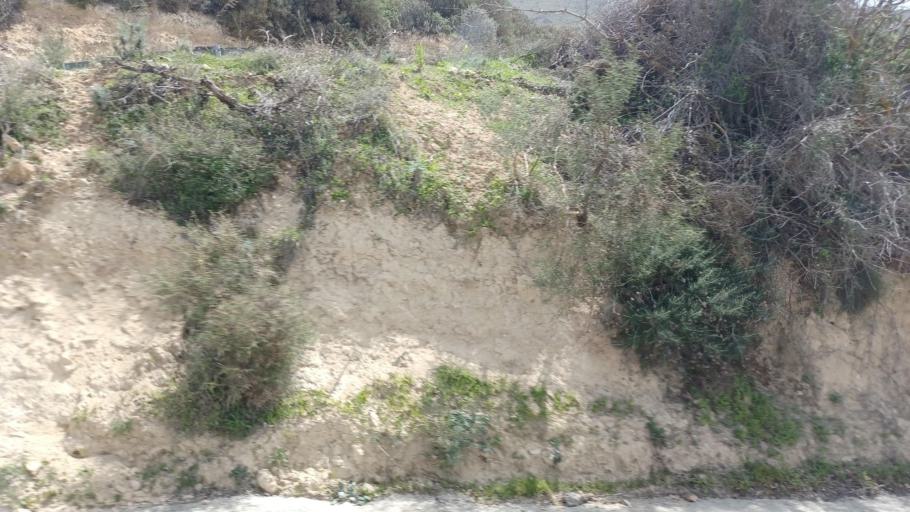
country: CY
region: Limassol
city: Pachna
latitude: 34.7721
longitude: 32.7509
